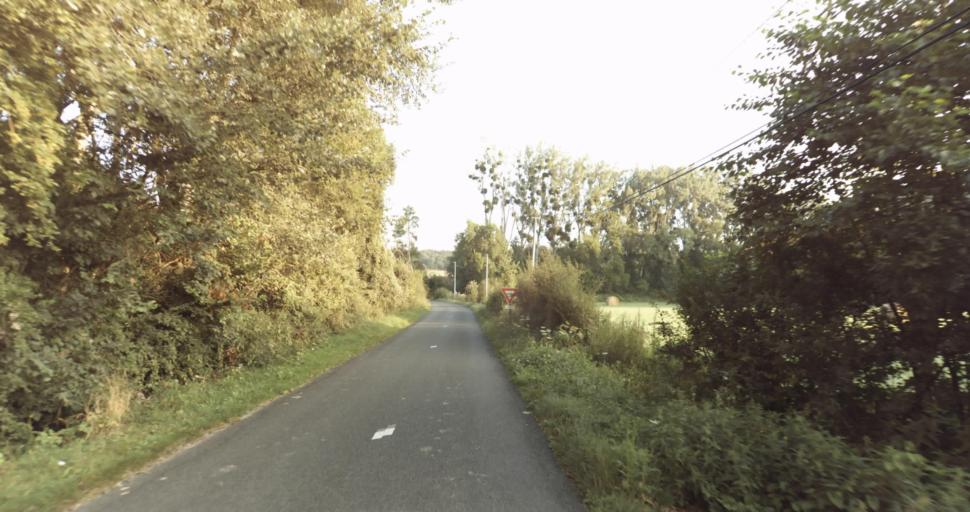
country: FR
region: Haute-Normandie
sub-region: Departement de l'Eure
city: Marcilly-sur-Eure
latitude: 48.7782
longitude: 1.3424
